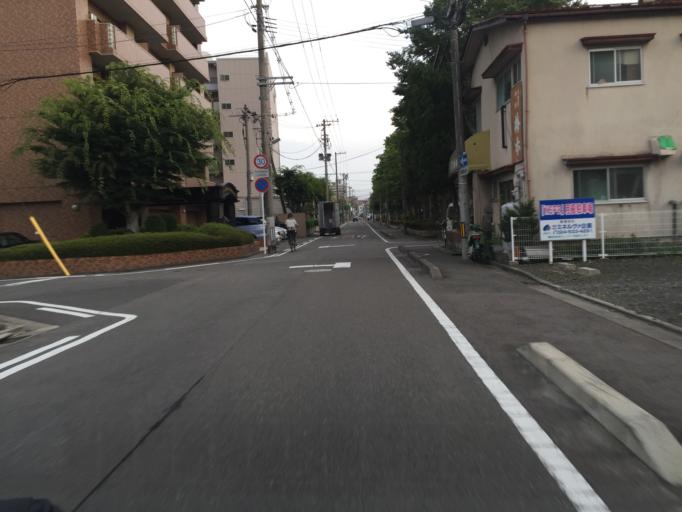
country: JP
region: Fukushima
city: Fukushima-shi
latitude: 37.7628
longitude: 140.4708
